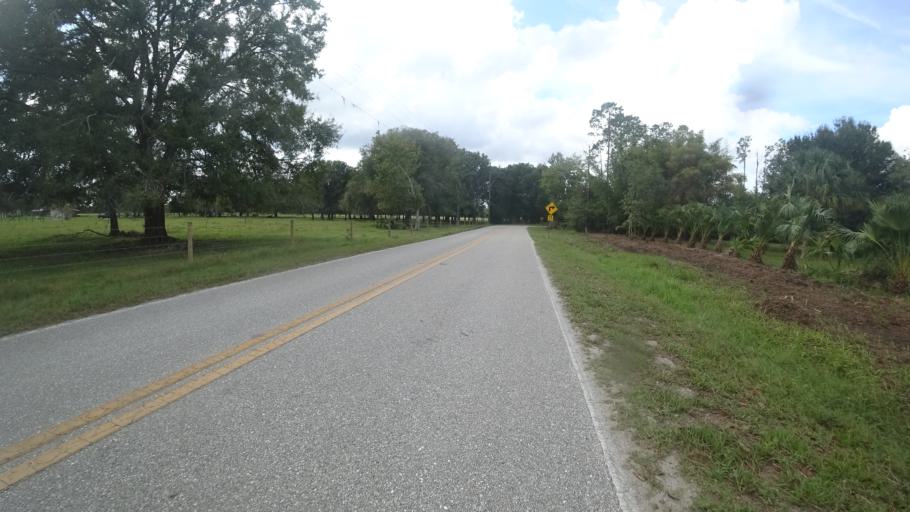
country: US
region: Florida
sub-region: Hillsborough County
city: Wimauma
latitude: 27.5972
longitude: -82.2070
